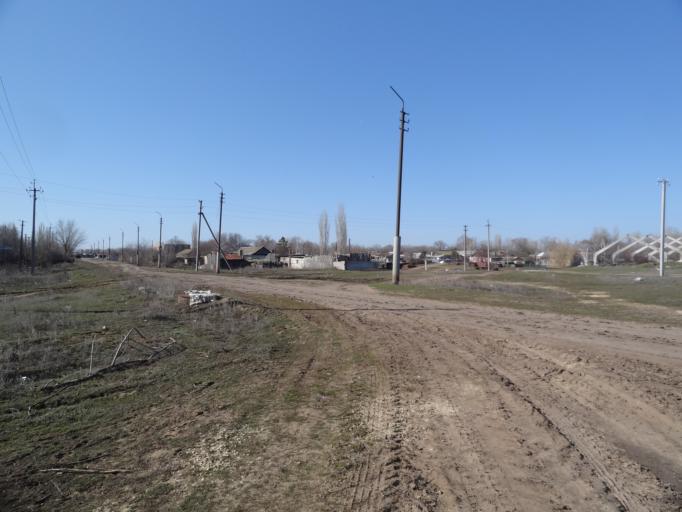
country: RU
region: Saratov
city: Shumeyka
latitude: 51.3928
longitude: 46.3041
